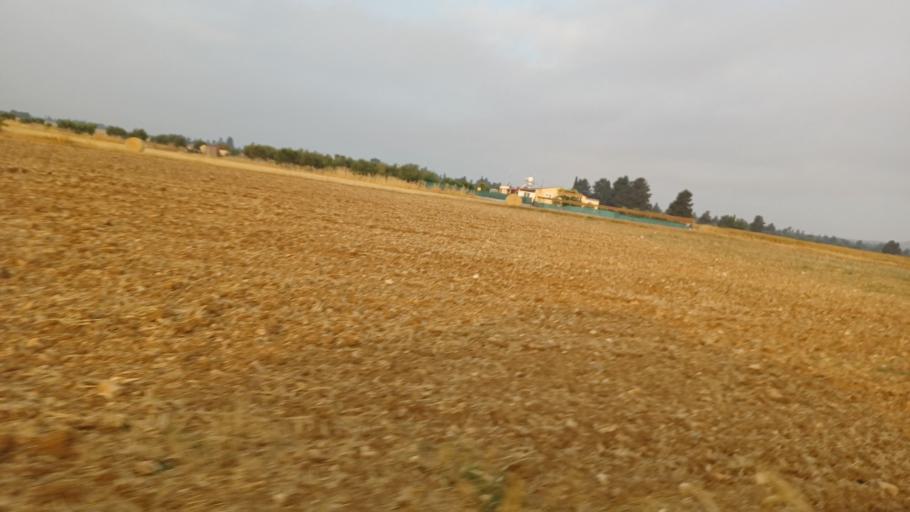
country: CY
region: Larnaka
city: Tersefanou
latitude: 34.8278
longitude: 33.5183
